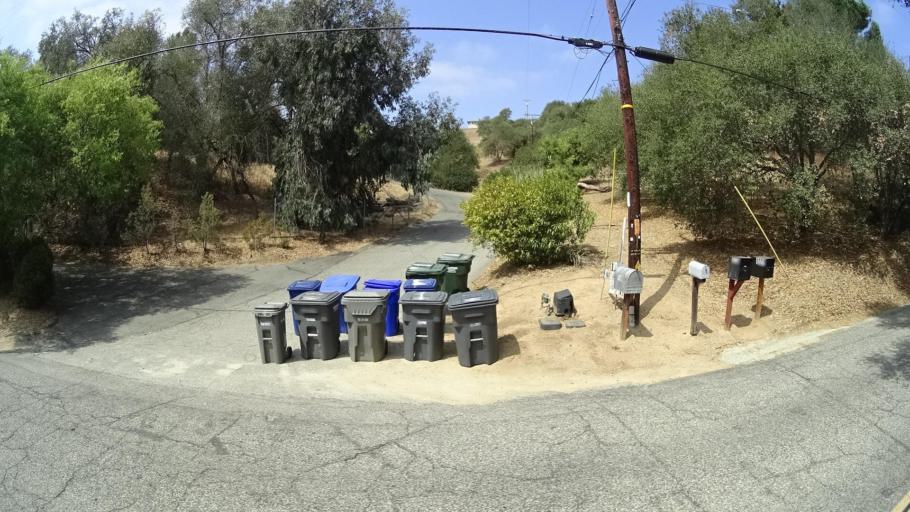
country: US
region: California
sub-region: San Diego County
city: Fallbrook
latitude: 33.3711
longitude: -117.2084
